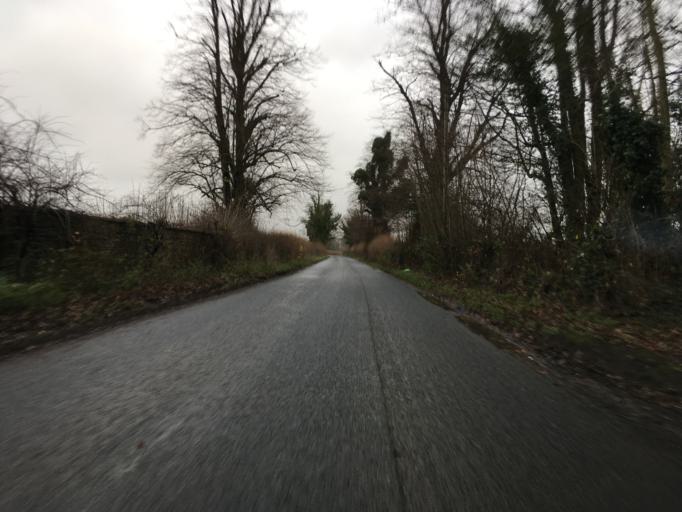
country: GB
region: England
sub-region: Wiltshire
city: Nettleton
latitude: 51.5152
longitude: -2.2295
